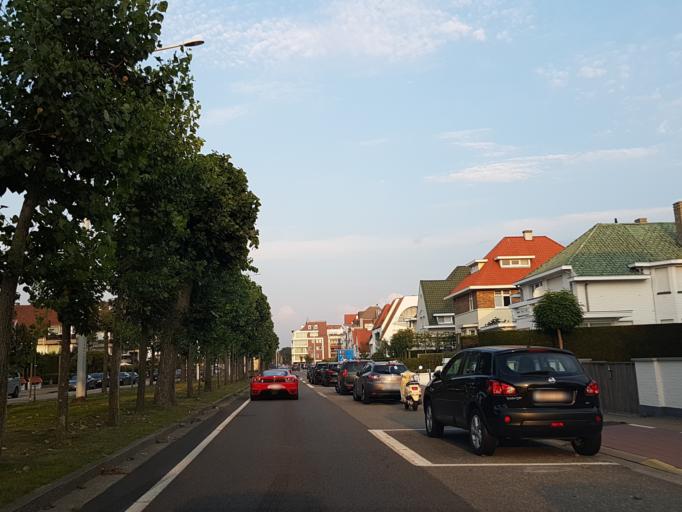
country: BE
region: Flanders
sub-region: Provincie West-Vlaanderen
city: Knokke-Heist
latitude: 51.3470
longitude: 3.2818
